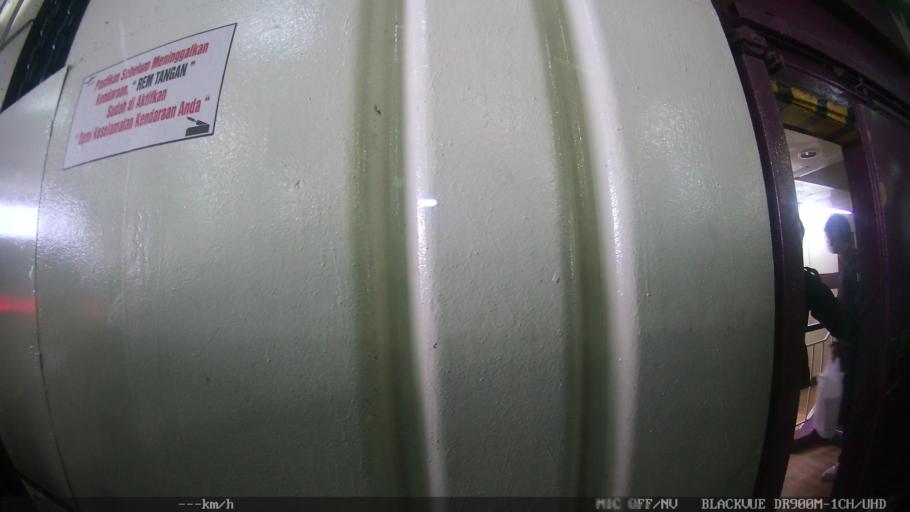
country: ID
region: Lampung
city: Penengahan
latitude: -5.8652
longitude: 105.7570
